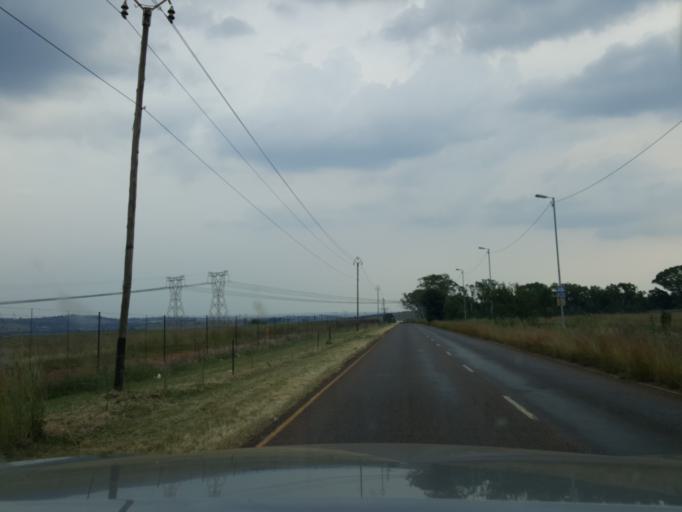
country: ZA
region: Gauteng
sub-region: City of Tshwane Metropolitan Municipality
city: Centurion
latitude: -25.8510
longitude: 28.2754
